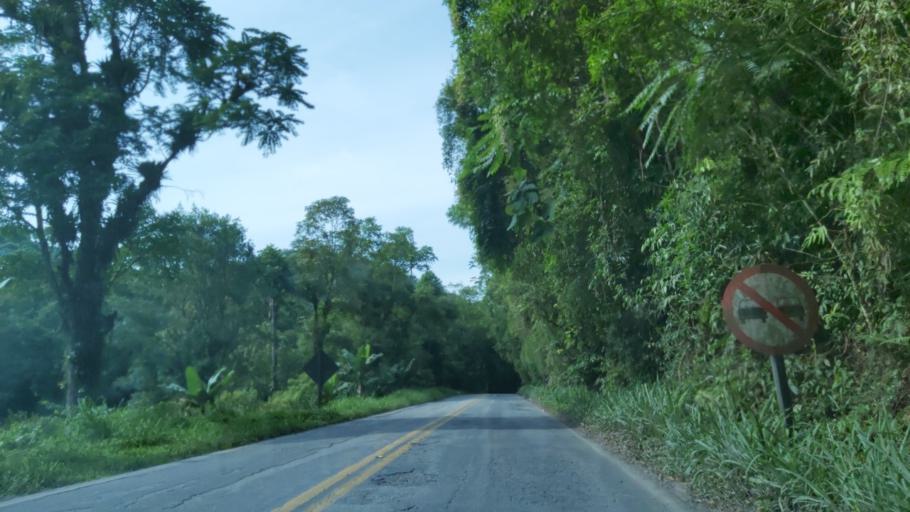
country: BR
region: Sao Paulo
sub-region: Miracatu
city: Miracatu
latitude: -24.0551
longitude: -47.5769
